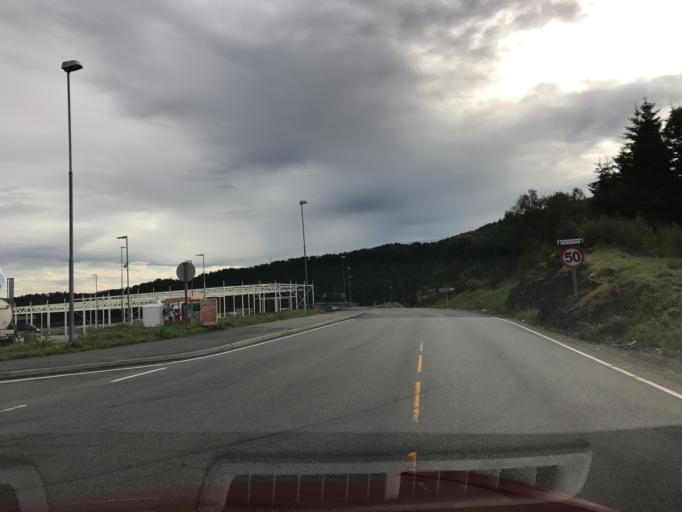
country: NO
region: Hordaland
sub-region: Bergen
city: Hylkje
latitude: 60.4843
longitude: 5.3767
